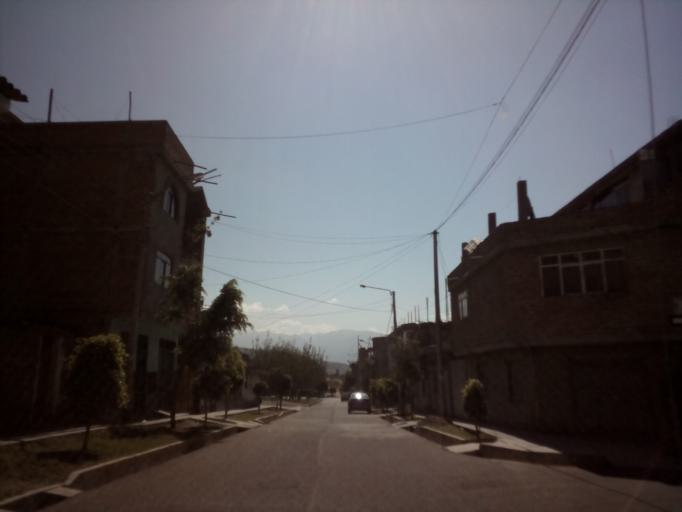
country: PE
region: Ayacucho
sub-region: Provincia de Huamanga
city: Ayacucho
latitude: -13.1454
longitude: -74.2273
